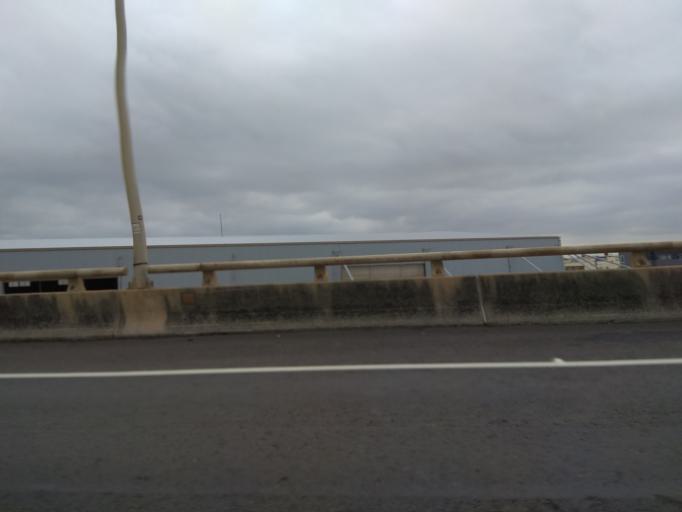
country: TW
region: Taiwan
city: Taoyuan City
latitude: 25.1089
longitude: 121.2302
